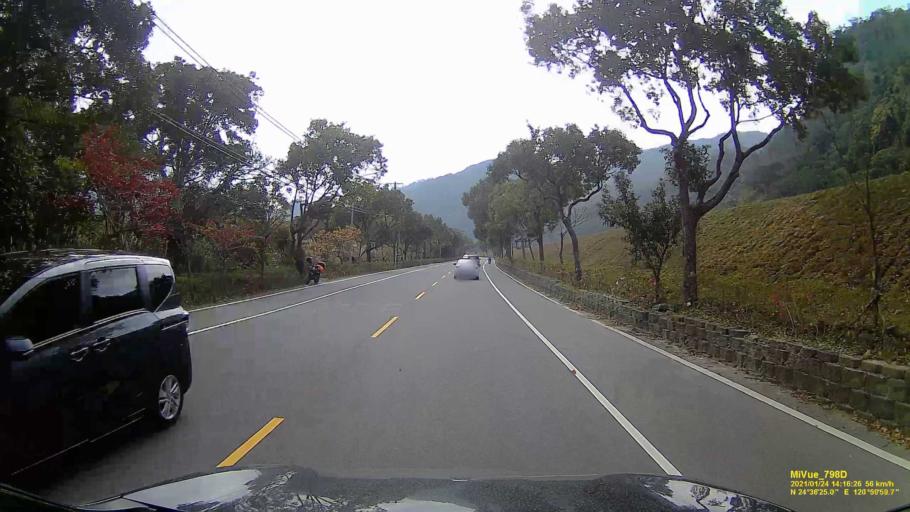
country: TW
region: Taiwan
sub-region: Miaoli
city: Miaoli
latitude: 24.6067
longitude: 120.9997
